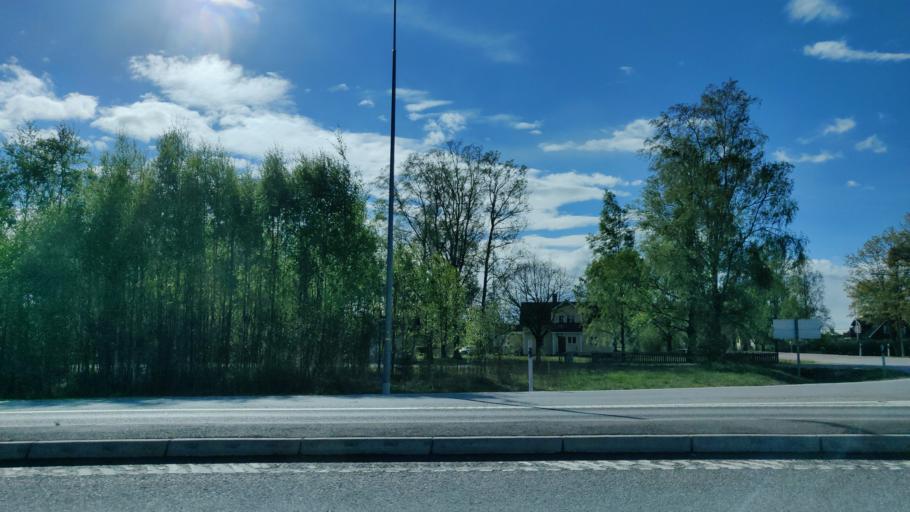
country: SE
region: Vaermland
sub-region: Forshaga Kommun
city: Forshaga
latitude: 59.4579
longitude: 13.4167
